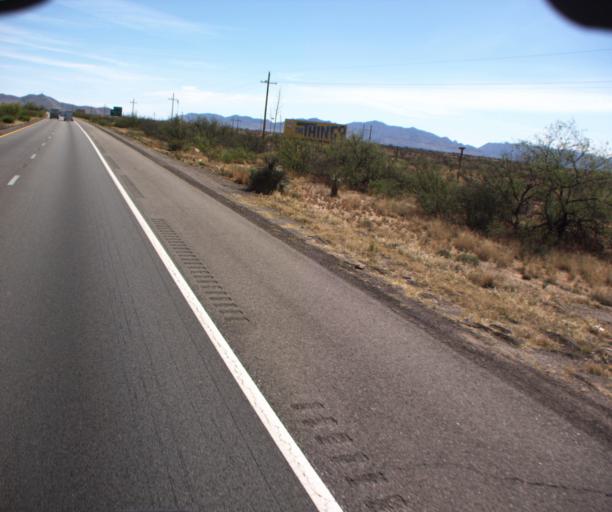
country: US
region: Arizona
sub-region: Cochise County
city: Saint David
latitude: 31.9850
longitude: -110.1977
